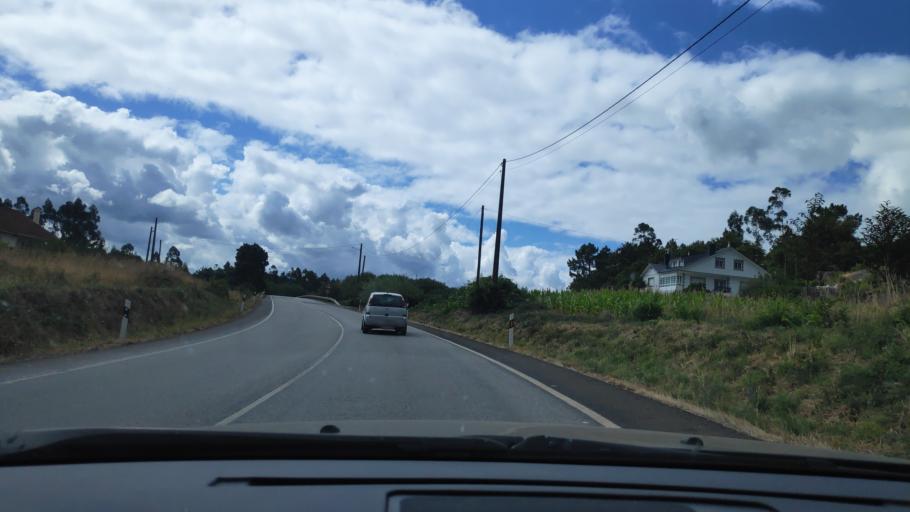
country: ES
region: Galicia
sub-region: Provincia de Pontevedra
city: Portas
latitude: 42.5901
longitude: -8.6921
